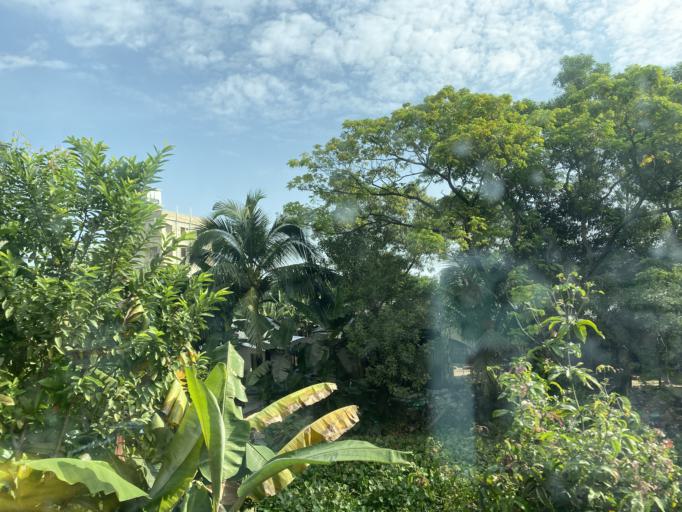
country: BD
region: Dhaka
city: Bhairab Bazar
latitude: 23.9661
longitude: 91.1165
